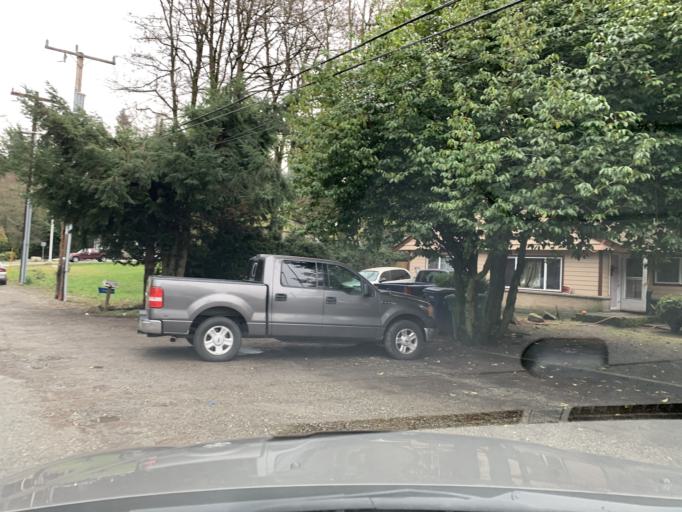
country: US
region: Washington
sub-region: King County
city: SeaTac
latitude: 47.4614
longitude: -122.2823
